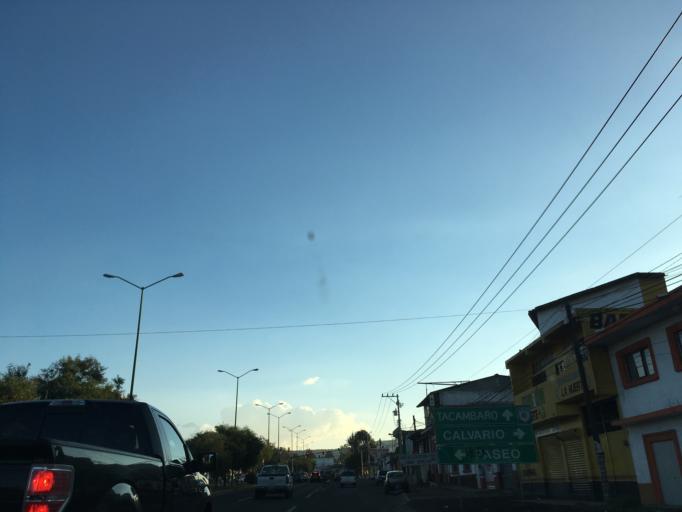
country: MX
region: Michoacan
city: Patzcuaro
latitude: 19.5149
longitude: -101.6184
